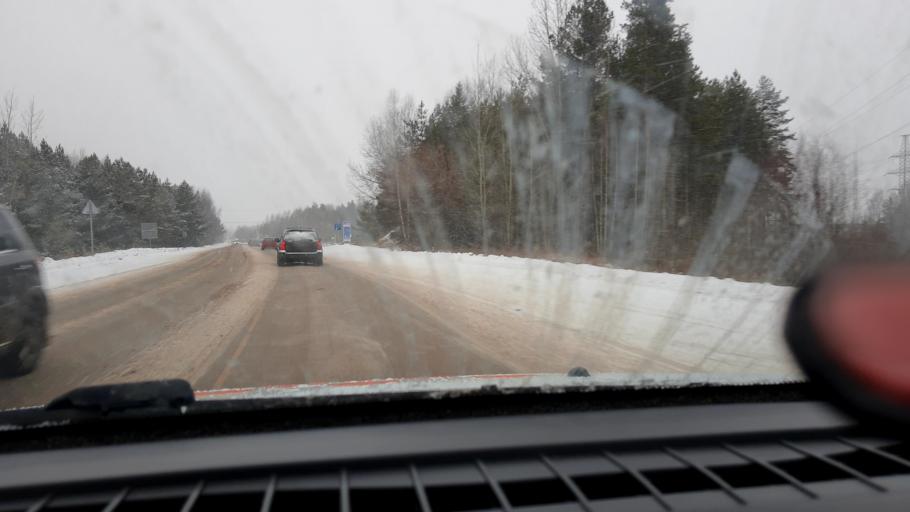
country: RU
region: Nizjnij Novgorod
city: Bor
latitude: 56.3242
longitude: 44.1439
